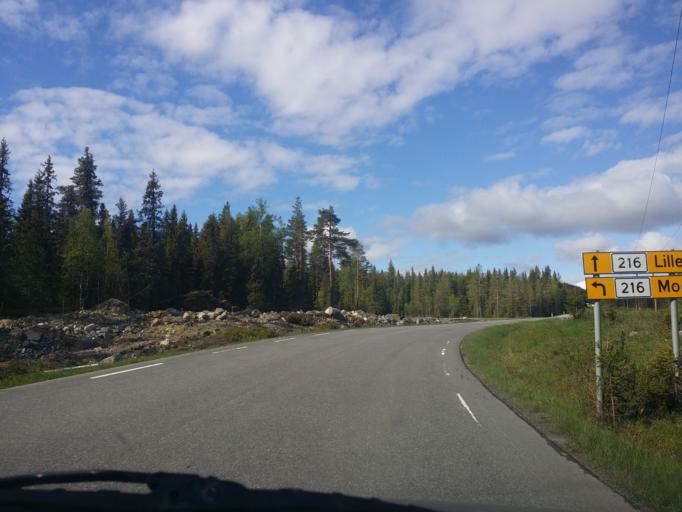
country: NO
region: Hedmark
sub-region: Ringsaker
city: Moelv
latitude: 61.0969
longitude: 10.6816
